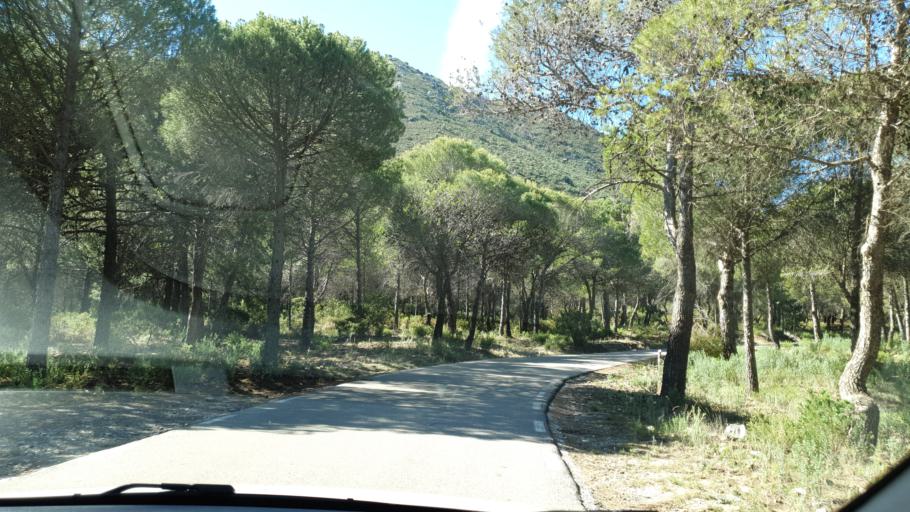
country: ES
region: Andalusia
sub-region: Provincia de Malaga
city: Ojen
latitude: 36.5883
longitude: -4.8583
